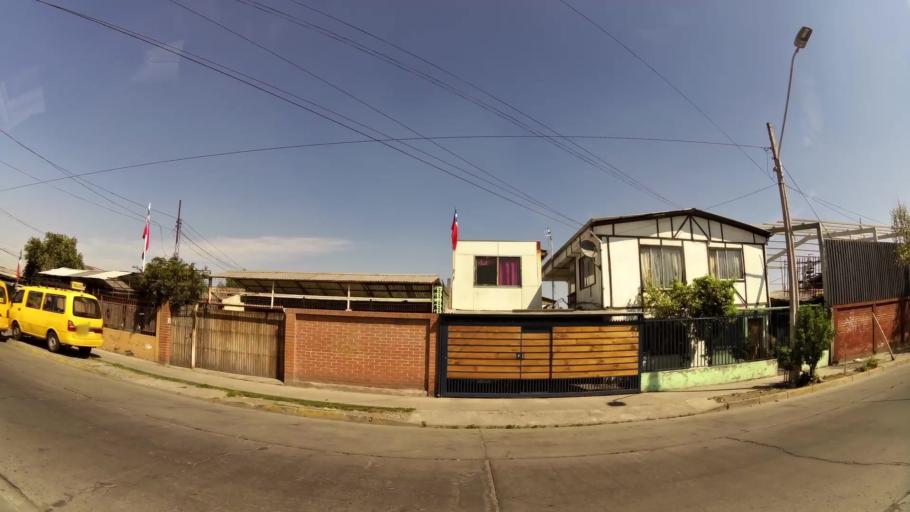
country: CL
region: Santiago Metropolitan
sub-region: Provincia de Santiago
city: La Pintana
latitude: -33.5235
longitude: -70.6460
